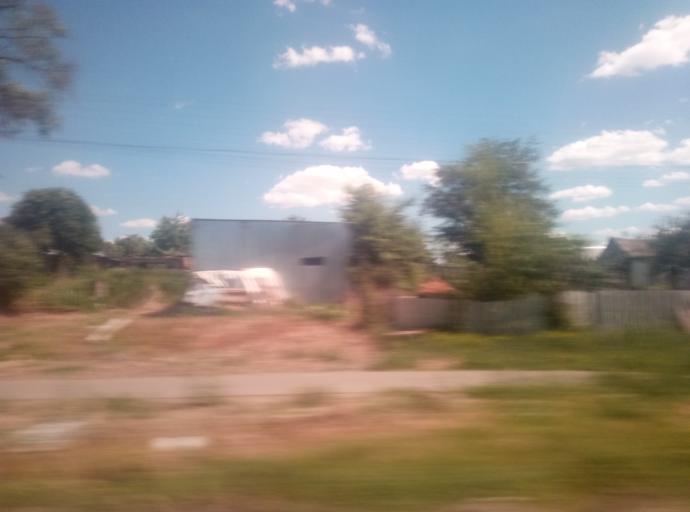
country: RU
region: Tula
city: Kireyevsk
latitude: 53.9866
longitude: 37.9320
